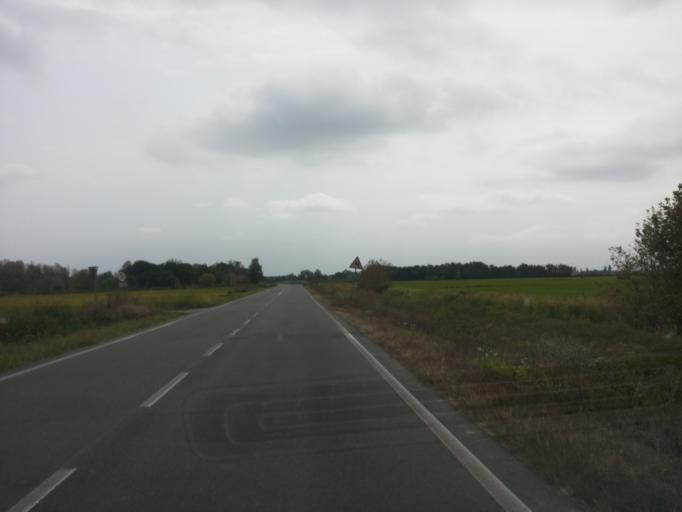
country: IT
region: Piedmont
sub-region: Provincia di Vercelli
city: Prarolo
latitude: 45.3004
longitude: 8.4604
